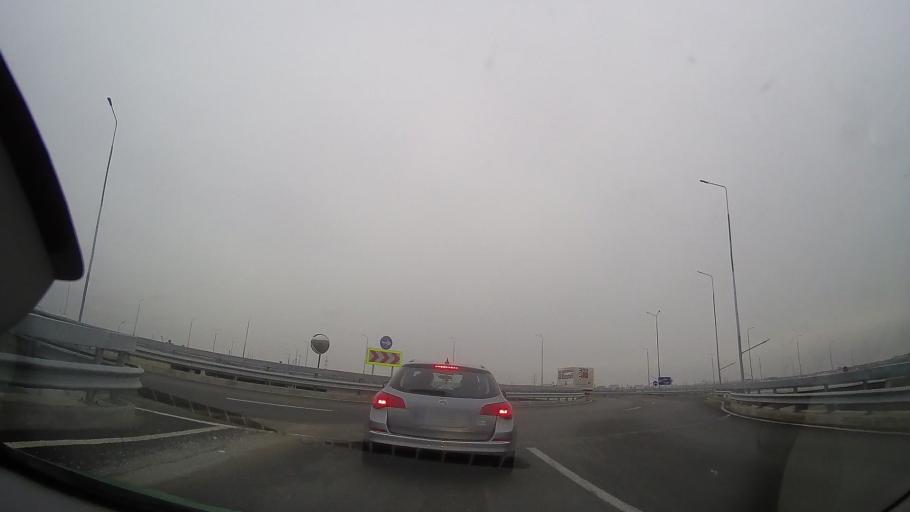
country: RO
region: Prahova
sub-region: Comuna Paulesti
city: Paulesti
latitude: 44.9775
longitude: 25.9917
